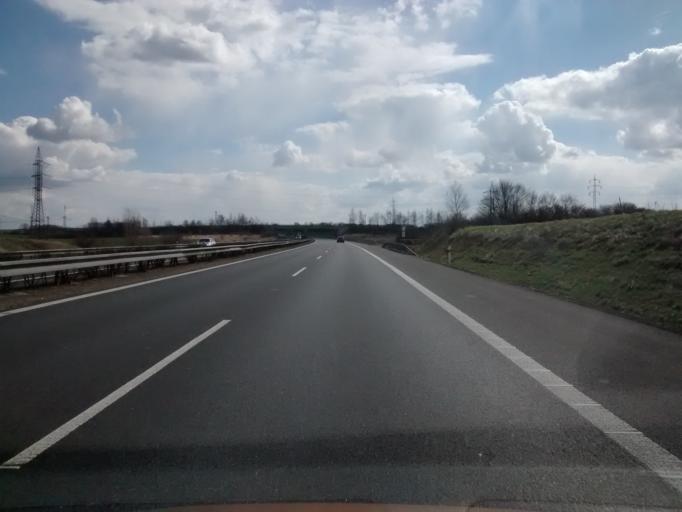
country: CZ
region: Central Bohemia
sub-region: Okres Melnik
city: Veltrusy
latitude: 50.2814
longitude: 14.3529
